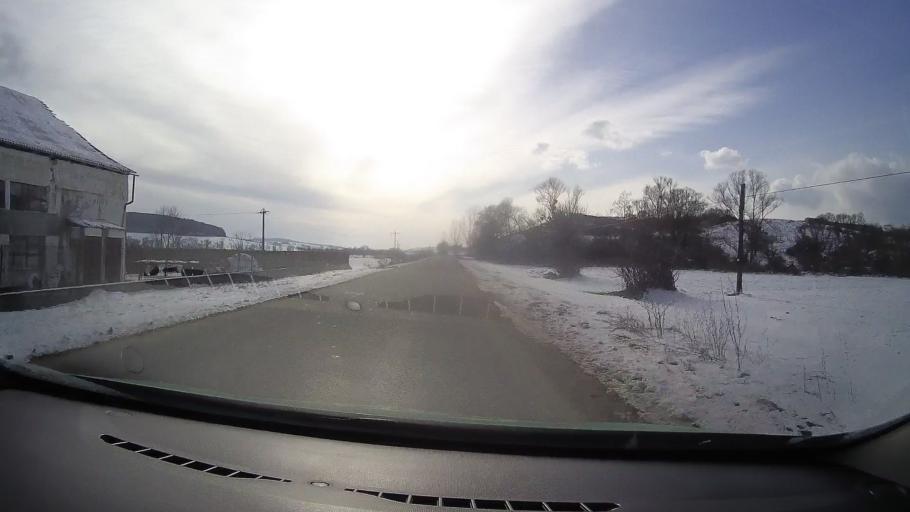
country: RO
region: Sibiu
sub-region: Comuna Iacobeni
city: Iacobeni
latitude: 46.0395
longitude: 24.7302
